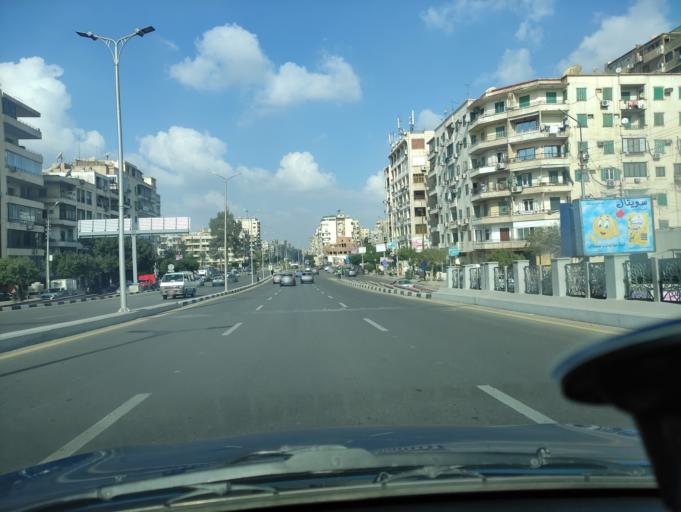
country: EG
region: Muhafazat al Qahirah
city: Cairo
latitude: 30.0984
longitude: 31.3428
